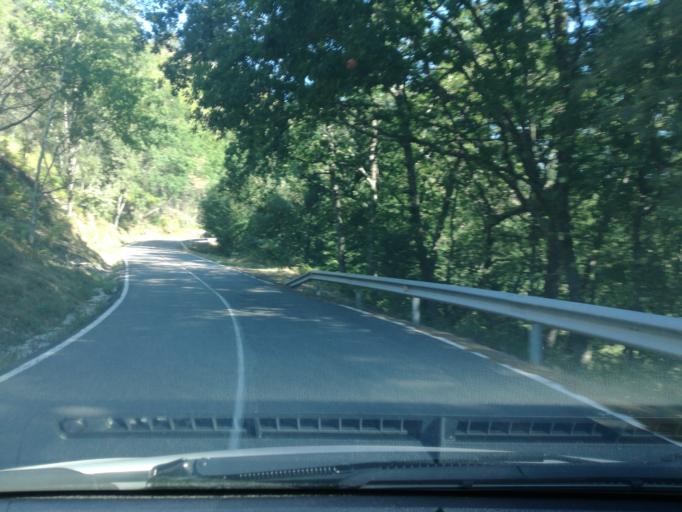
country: ES
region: Galicia
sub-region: Provincia de Ourense
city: Lobios
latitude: 41.8520
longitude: -8.1137
